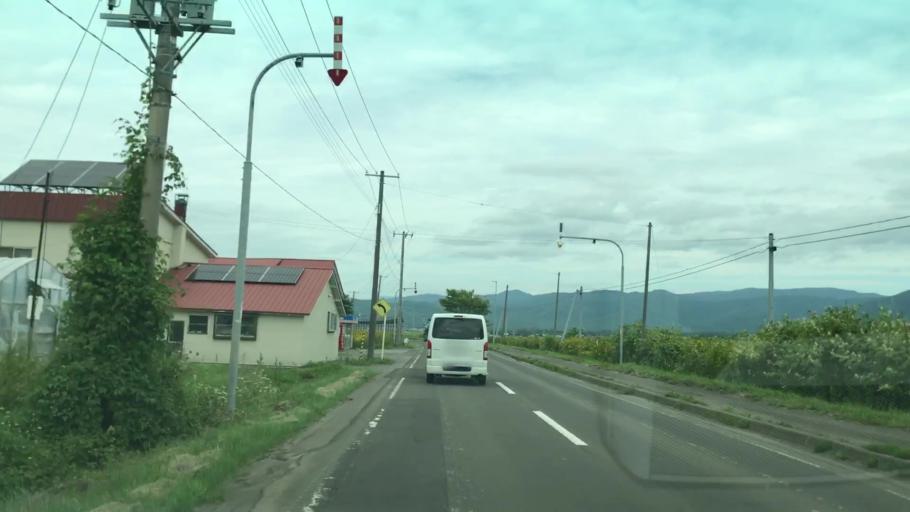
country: JP
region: Hokkaido
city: Iwanai
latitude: 43.0035
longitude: 140.5849
